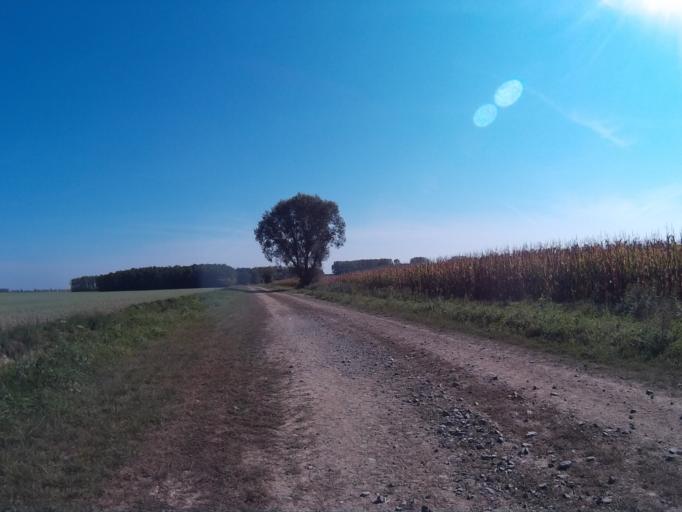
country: HU
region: Vas
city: Kormend
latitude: 47.0739
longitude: 16.6294
